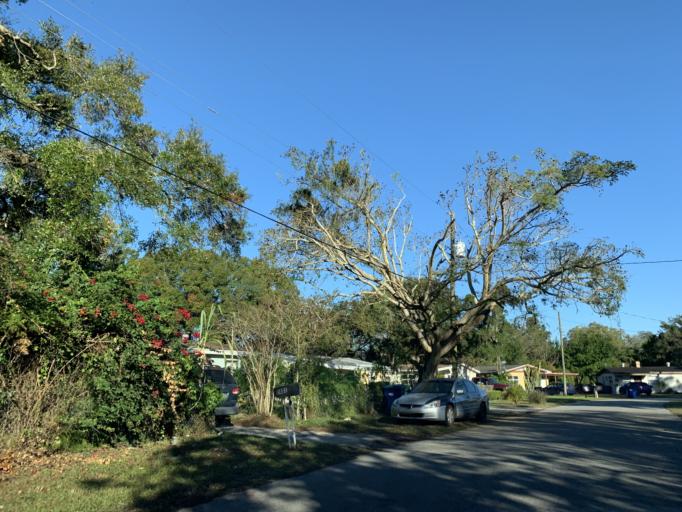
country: US
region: Florida
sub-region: Hillsborough County
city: University
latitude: 28.0349
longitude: -82.4336
